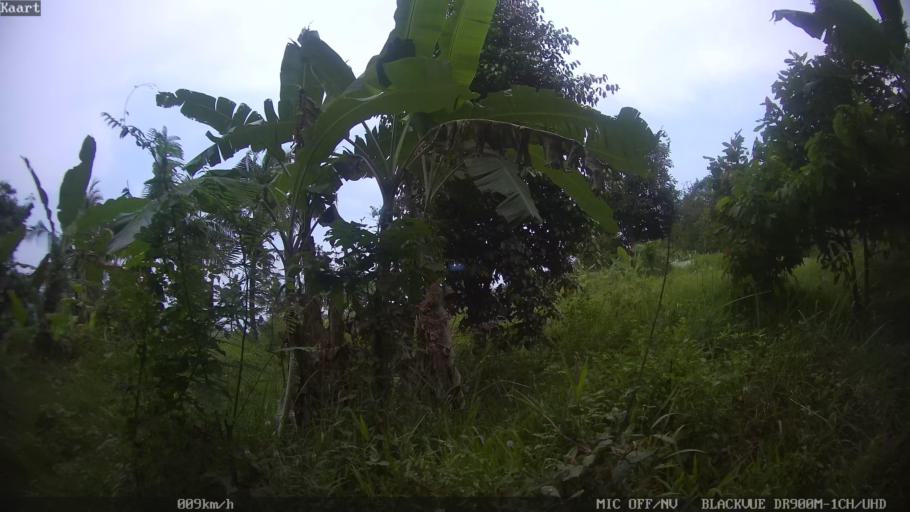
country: ID
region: Lampung
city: Panjang
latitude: -5.4305
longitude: 105.3360
